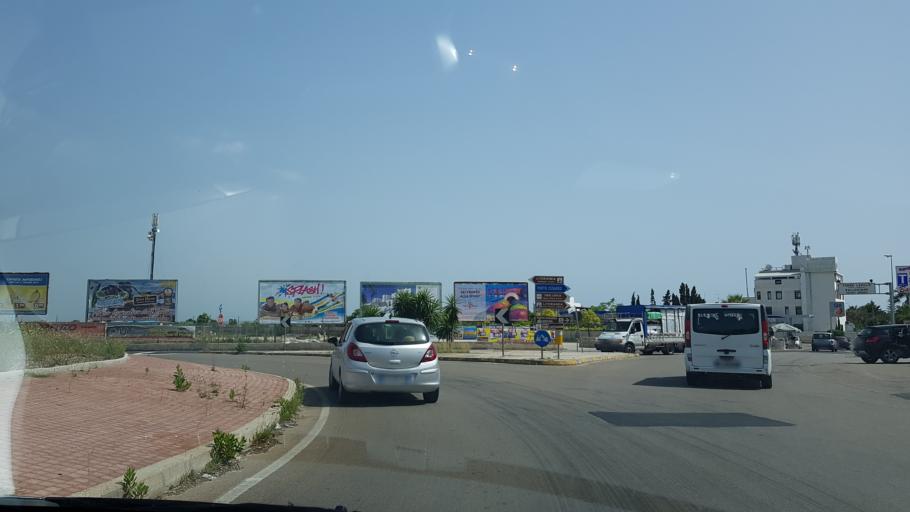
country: IT
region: Apulia
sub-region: Provincia di Lecce
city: Porto Cesareo
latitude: 40.2953
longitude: 17.8551
